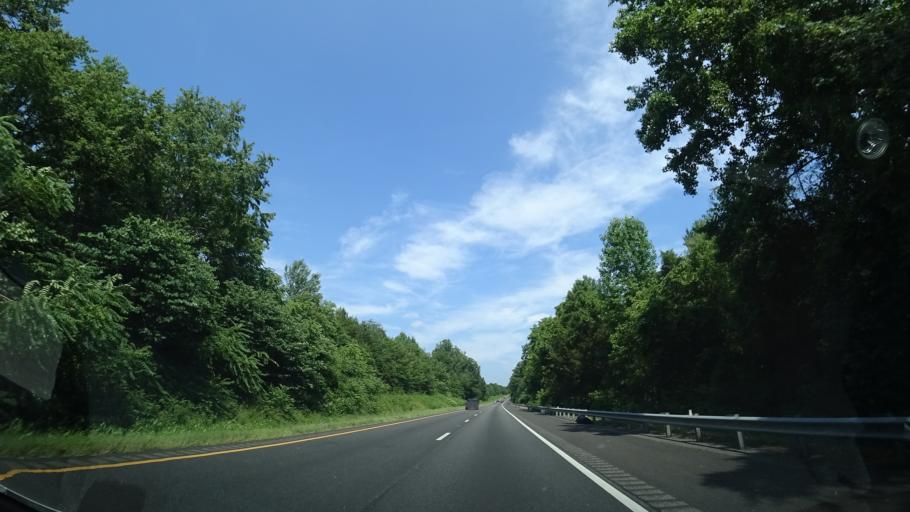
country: US
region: Virginia
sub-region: Fluvanna County
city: Lake Monticello
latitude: 37.9970
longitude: -78.2954
